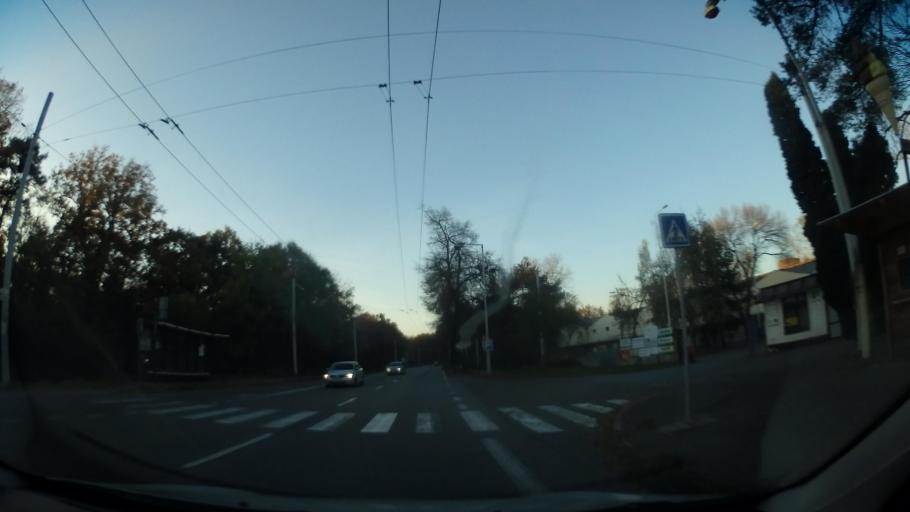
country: CZ
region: Pardubicky
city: Rybitvi
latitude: 50.0627
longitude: 15.7108
